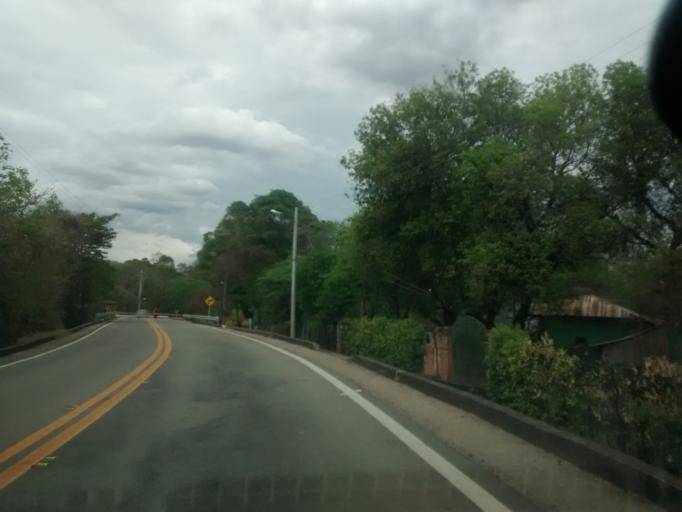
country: CO
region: Cundinamarca
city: Tocaima
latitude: 4.4419
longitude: -74.6736
